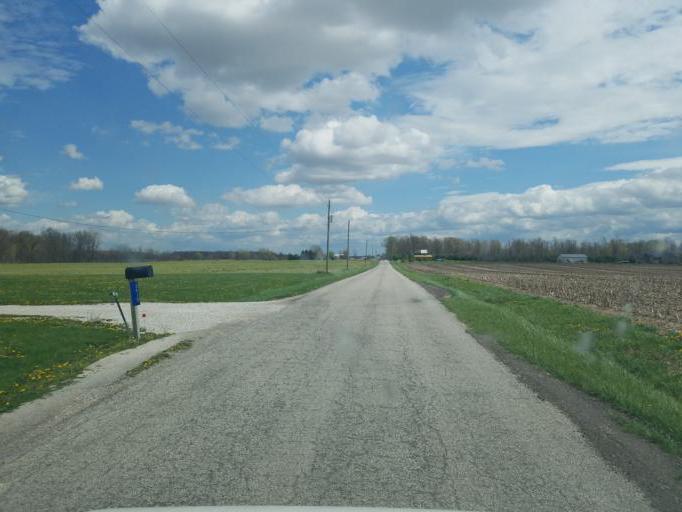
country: US
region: Ohio
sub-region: Crawford County
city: Bucyrus
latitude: 40.9067
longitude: -82.9493
